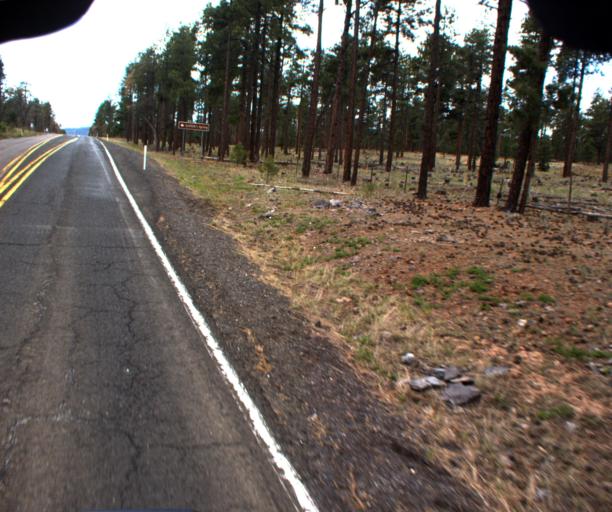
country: US
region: Arizona
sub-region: Coconino County
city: Kachina Village
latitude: 35.1169
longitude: -111.7108
